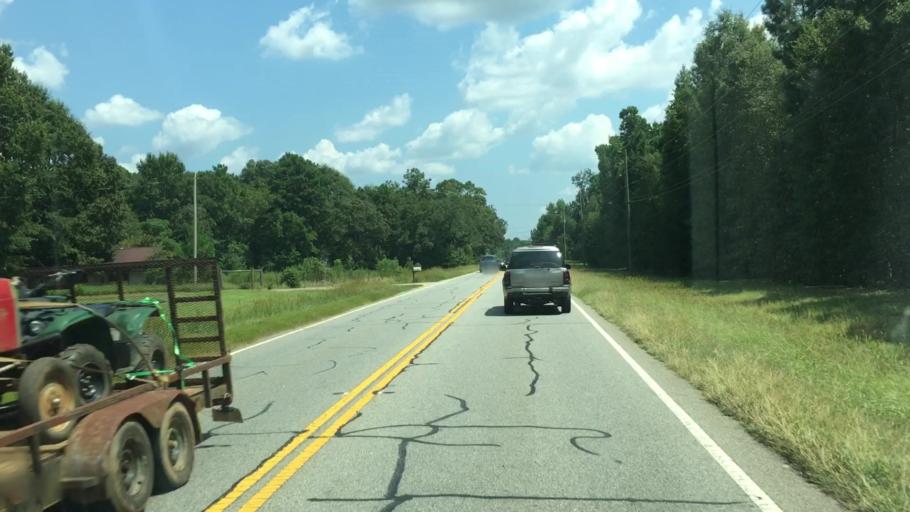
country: US
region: Georgia
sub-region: Barrow County
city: Statham
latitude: 33.9102
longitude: -83.5918
